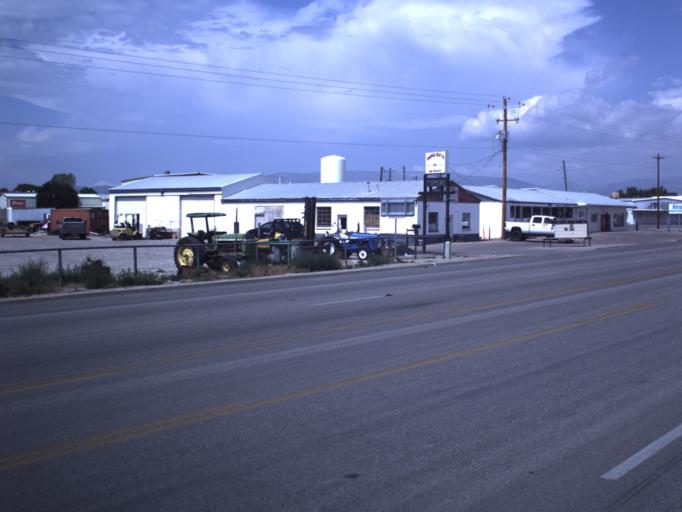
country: US
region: Utah
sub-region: Uintah County
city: Naples
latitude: 40.4478
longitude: -109.5013
